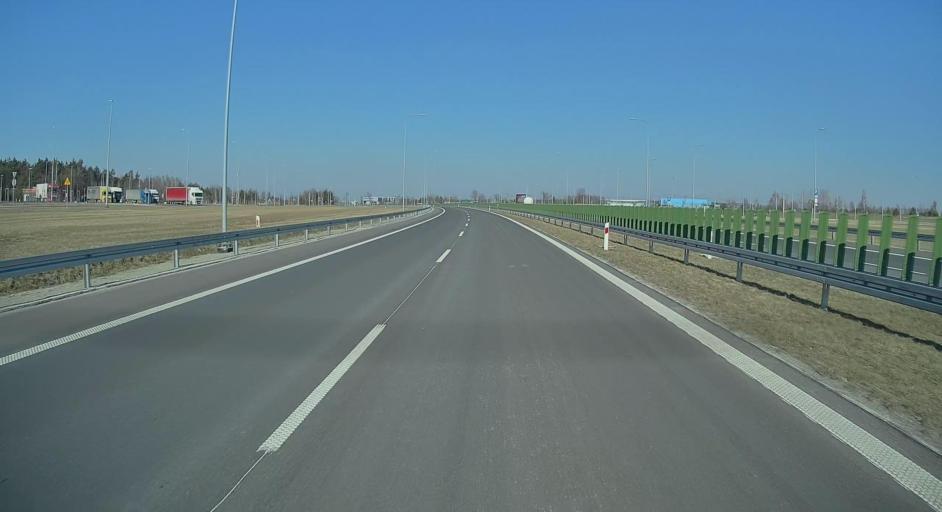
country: PL
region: Lublin Voivodeship
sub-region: Powiat janowski
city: Janow Lubelski
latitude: 50.7157
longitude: 22.3843
